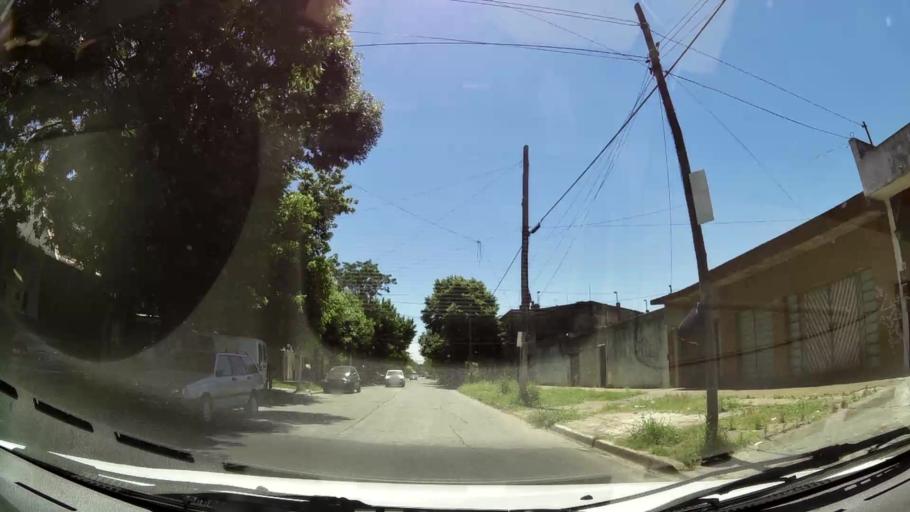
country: AR
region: Buenos Aires
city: Caseros
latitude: -34.5949
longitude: -58.5590
